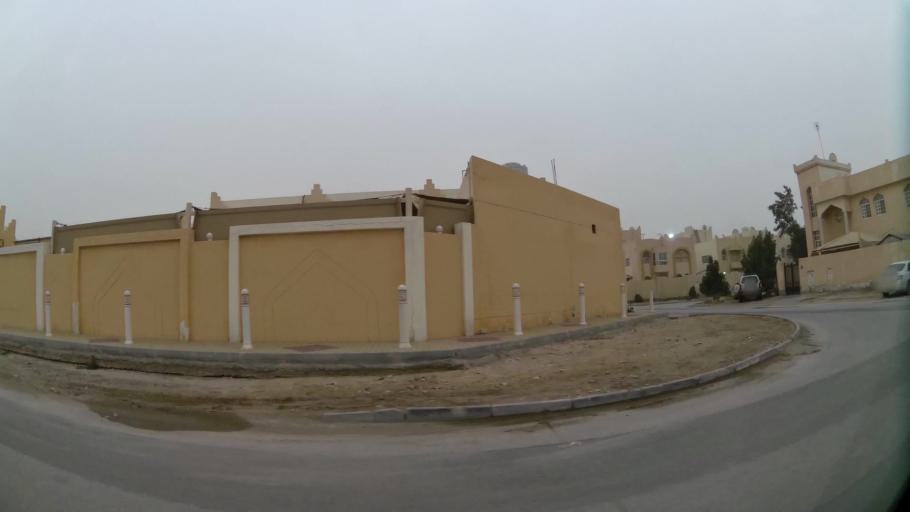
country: QA
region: Baladiyat ad Dawhah
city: Doha
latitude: 25.2355
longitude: 51.5002
